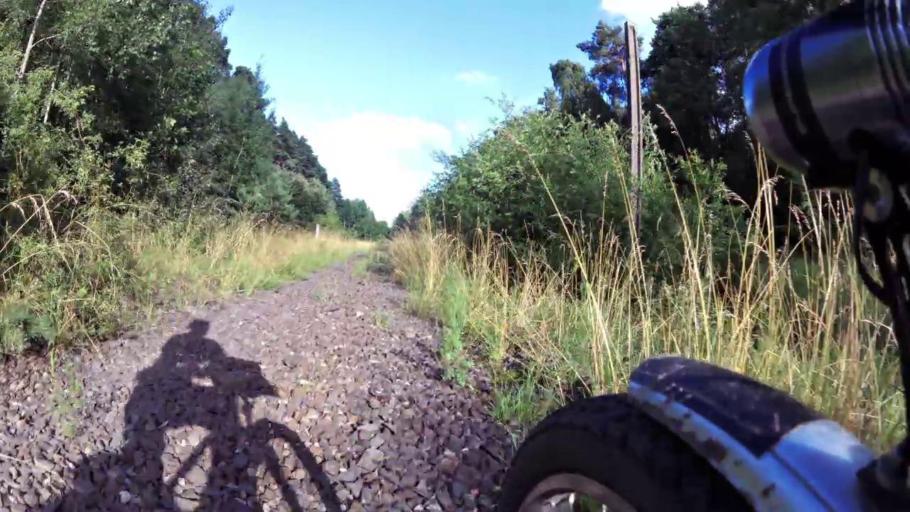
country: PL
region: West Pomeranian Voivodeship
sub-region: Powiat swidwinski
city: Swidwin
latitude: 53.7650
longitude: 15.8815
